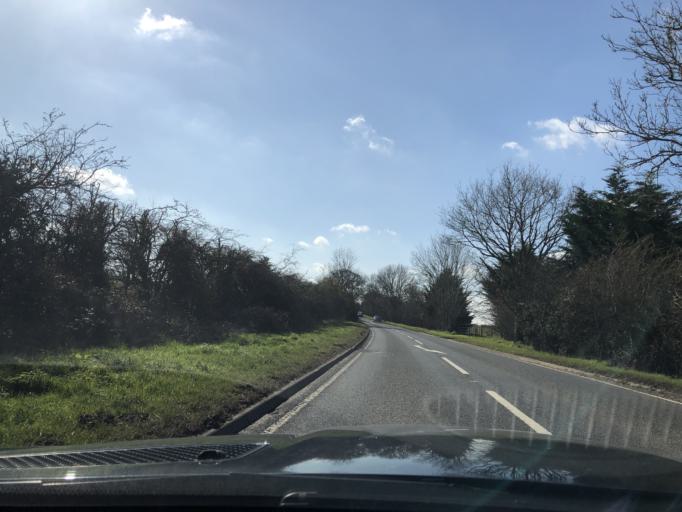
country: GB
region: England
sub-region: Warwickshire
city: Ryton on Dunsmore
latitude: 52.3250
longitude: -1.4190
